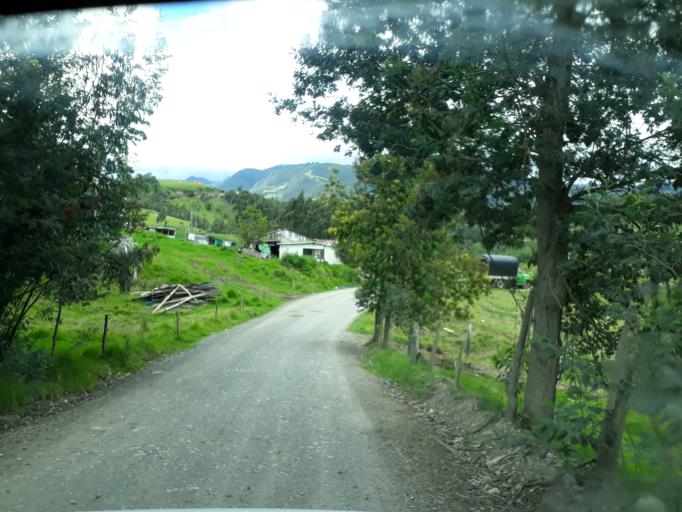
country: CO
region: Cundinamarca
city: Carmen de Carupa
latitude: 5.3077
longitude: -73.8988
